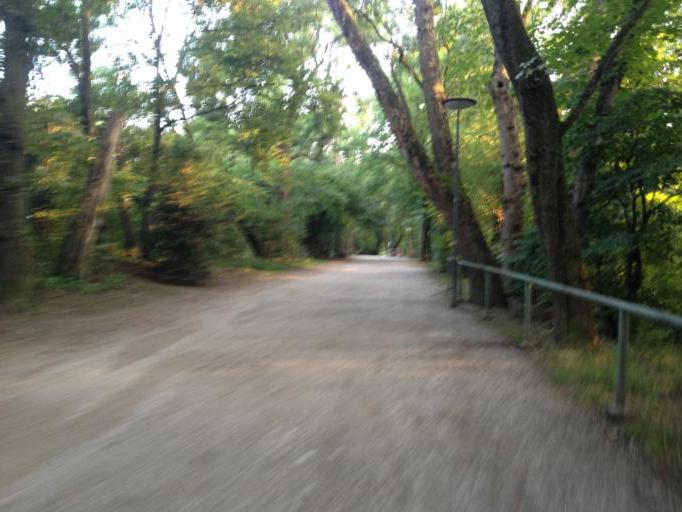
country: DE
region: Bavaria
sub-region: Upper Bavaria
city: Munich
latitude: 48.1347
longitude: 11.5916
